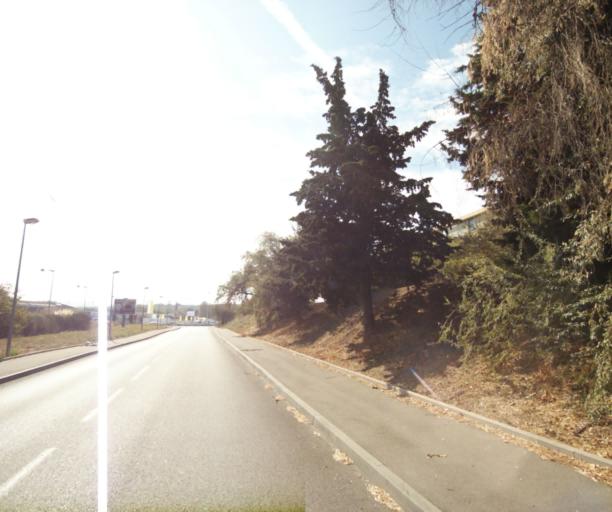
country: FR
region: Provence-Alpes-Cote d'Azur
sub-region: Departement des Bouches-du-Rhone
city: Saint-Victoret
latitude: 43.4202
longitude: 5.2284
